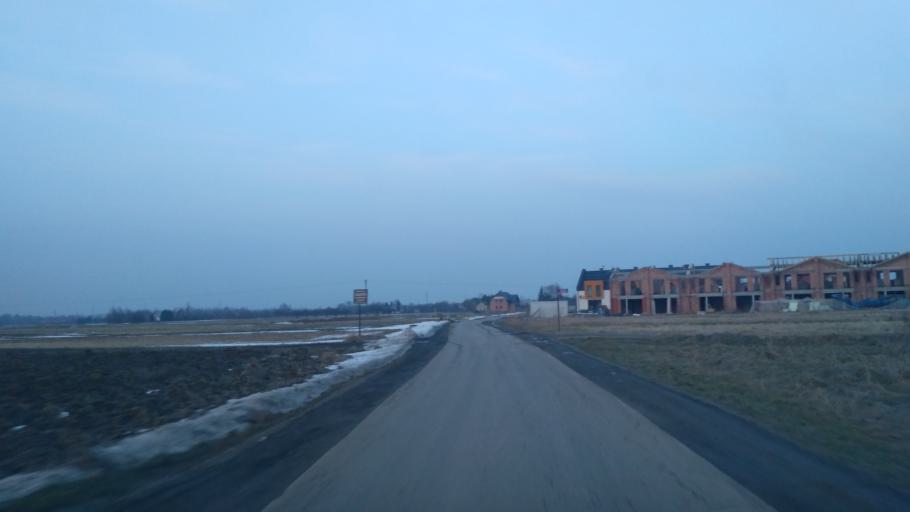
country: PL
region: Subcarpathian Voivodeship
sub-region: Powiat rzeszowski
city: Boguchwala
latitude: 49.9774
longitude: 21.9640
